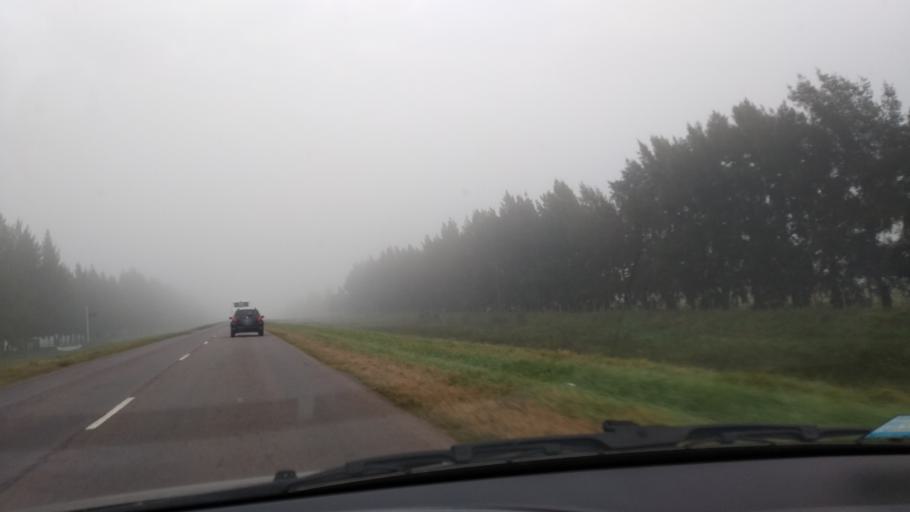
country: AR
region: Buenos Aires
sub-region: Partido de San Vicente
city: San Vicente
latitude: -35.2726
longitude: -58.5412
